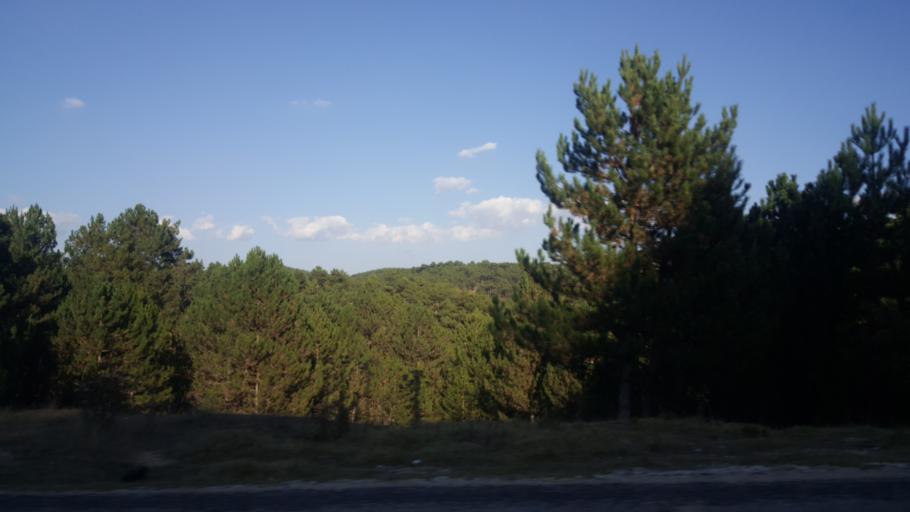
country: TR
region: Eskisehir
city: Kirka
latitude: 39.1145
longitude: 30.5885
